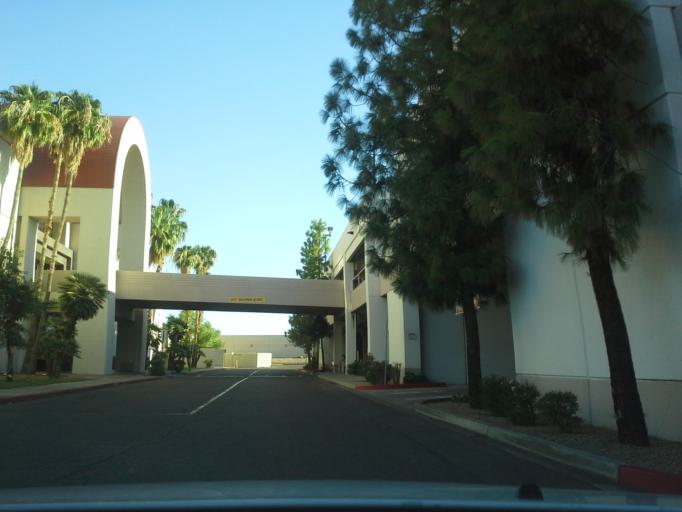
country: US
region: Arizona
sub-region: Maricopa County
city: Paradise Valley
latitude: 33.6041
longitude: -111.9824
